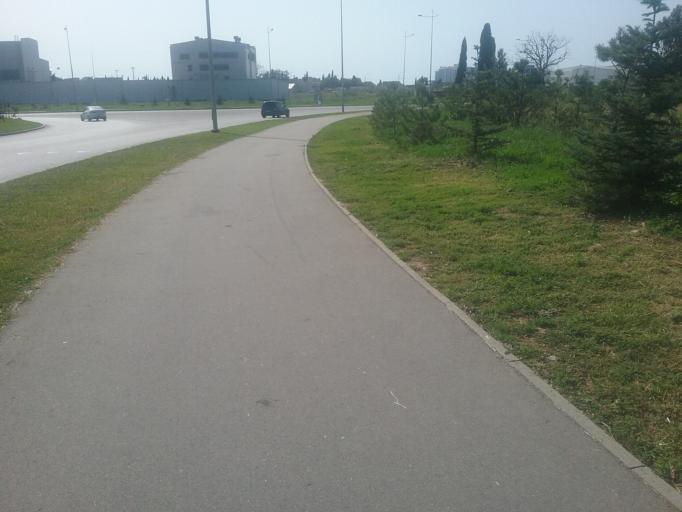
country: RU
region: Krasnodarskiy
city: Vysokoye
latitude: 43.3958
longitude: 39.9904
